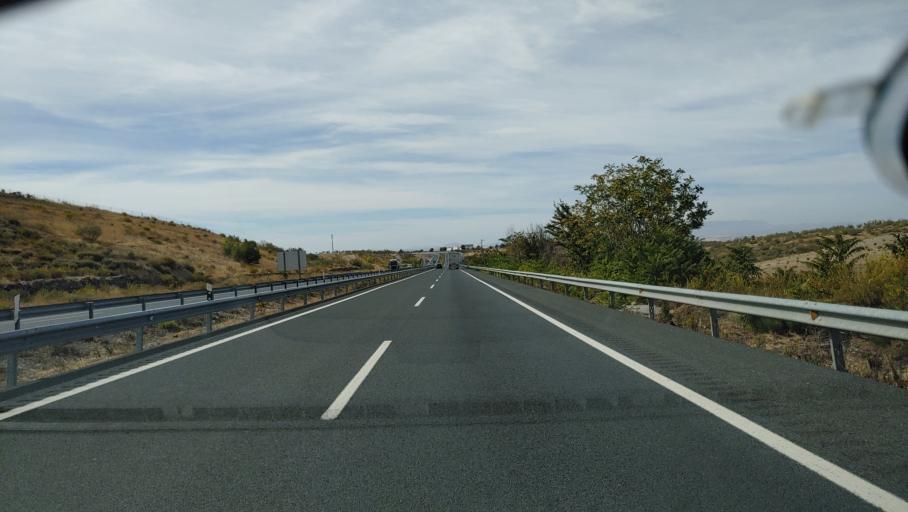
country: ES
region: Andalusia
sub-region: Provincia de Granada
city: Gor
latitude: 37.3960
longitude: -2.9773
